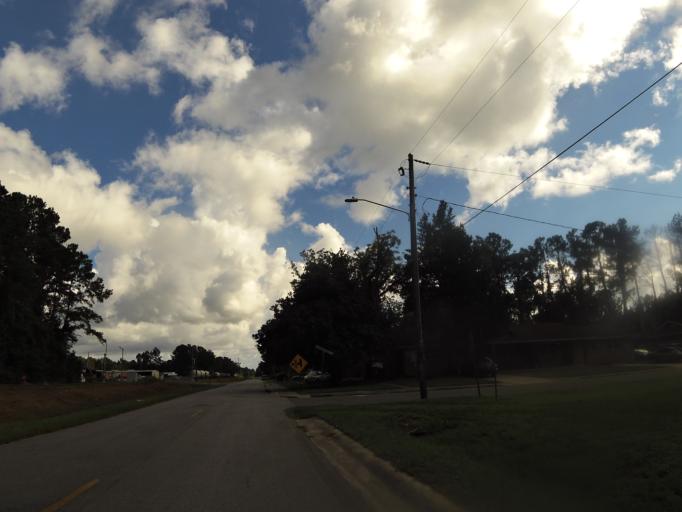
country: US
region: Georgia
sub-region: Camden County
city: Kingsland
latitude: 30.8119
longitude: -81.6938
